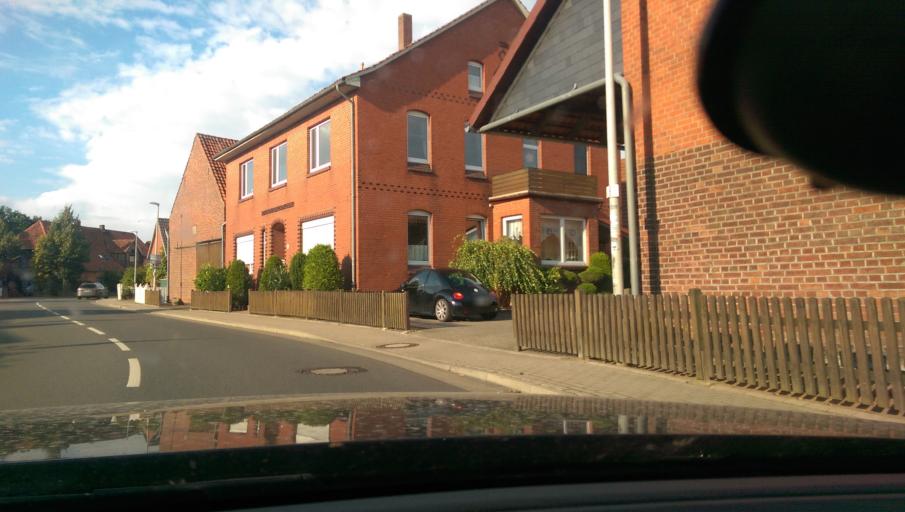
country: DE
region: Lower Saxony
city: Neustadt am Rubenberge
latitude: 52.5357
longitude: 9.4663
